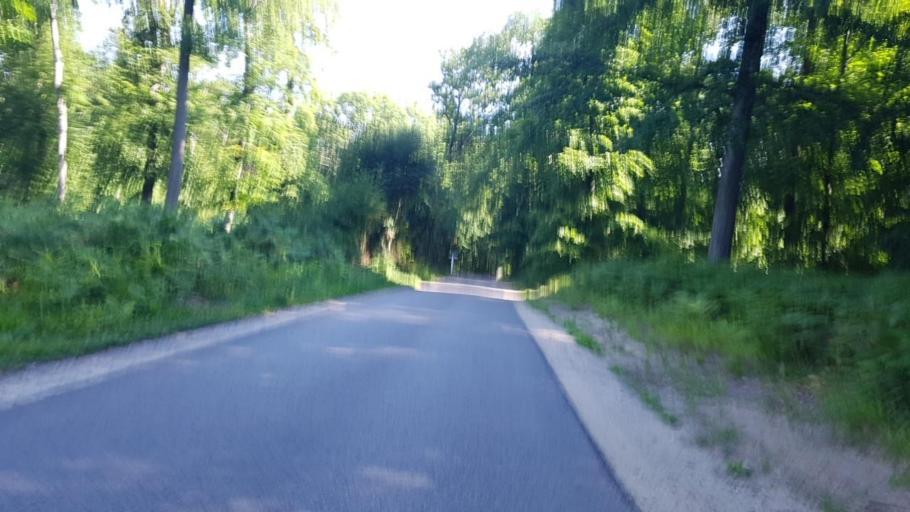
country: FR
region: Picardie
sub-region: Departement de l'Oise
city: Pont-Sainte-Maxence
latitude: 49.2845
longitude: 2.6235
